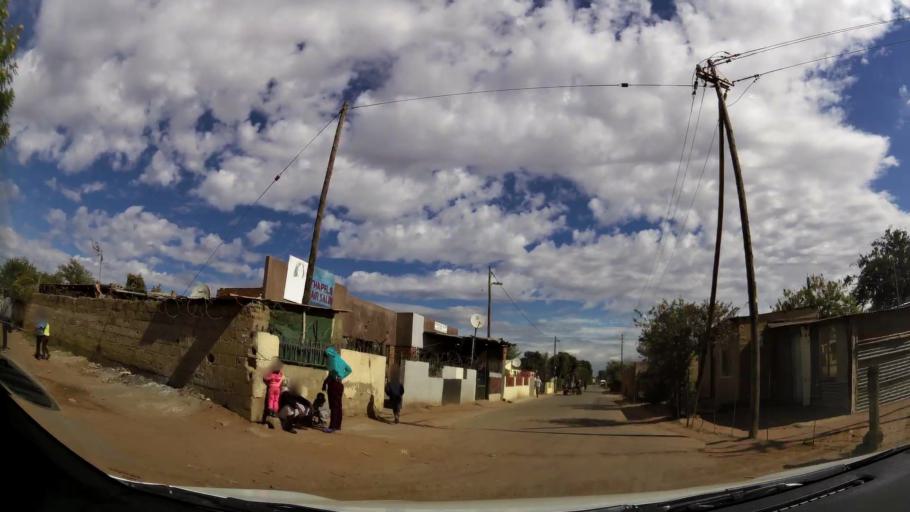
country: ZA
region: Limpopo
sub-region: Waterberg District Municipality
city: Bela-Bela
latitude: -24.8855
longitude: 28.3270
